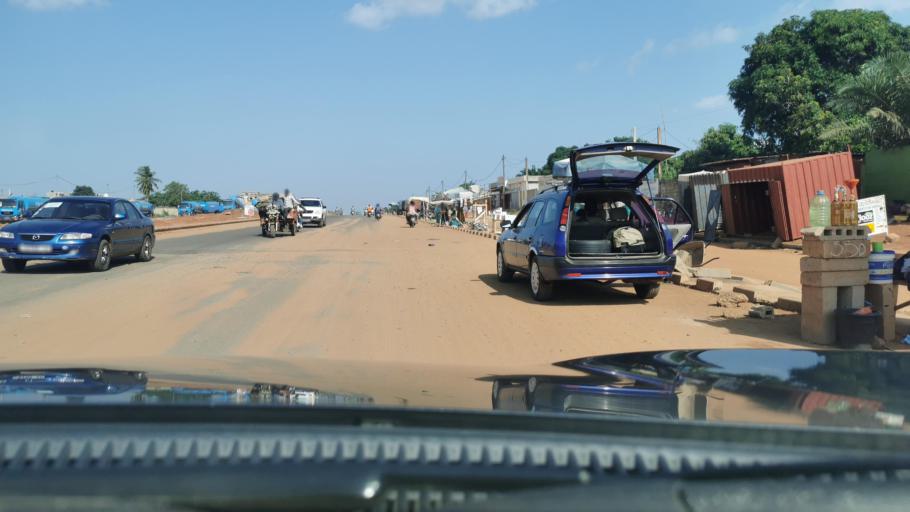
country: TG
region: Maritime
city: Lome
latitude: 6.2126
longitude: 1.1344
